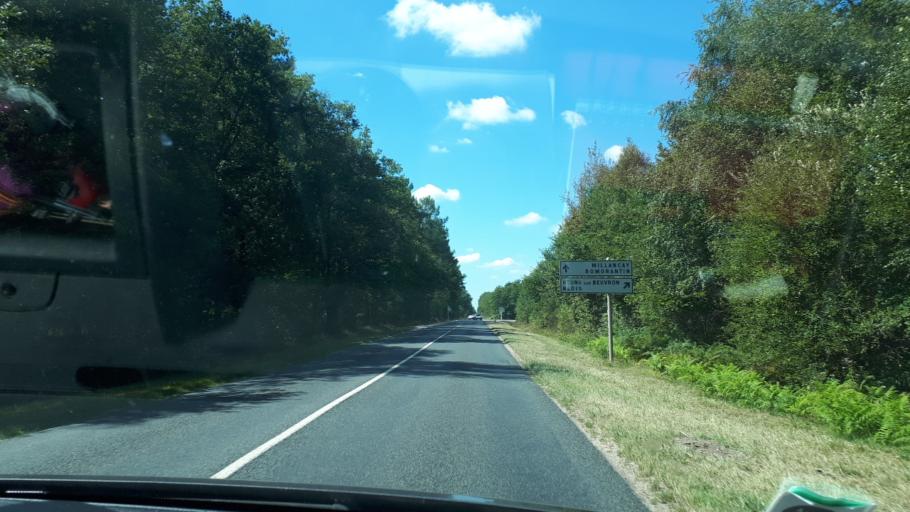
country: FR
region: Centre
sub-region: Departement du Loir-et-Cher
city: Neung-sur-Beuvron
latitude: 47.5351
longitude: 1.8372
